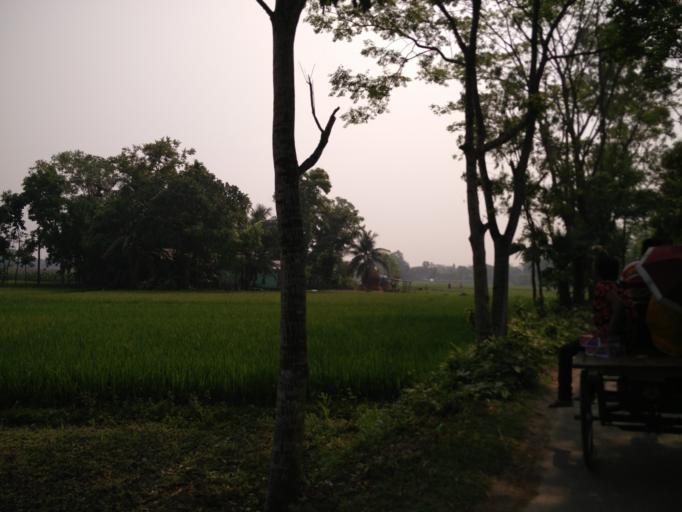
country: BD
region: Dhaka
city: Muktagacha
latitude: 24.9146
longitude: 90.2246
